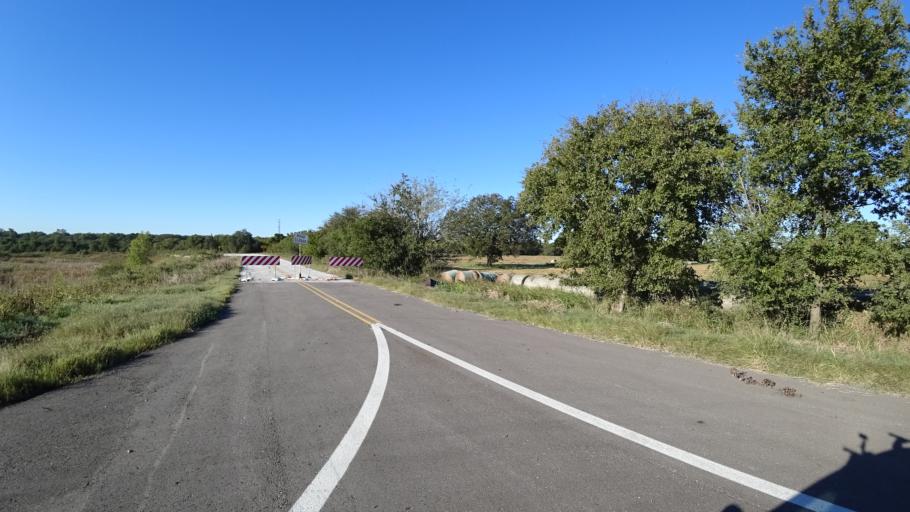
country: US
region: Texas
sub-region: Travis County
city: Hornsby Bend
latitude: 30.2137
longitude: -97.6393
